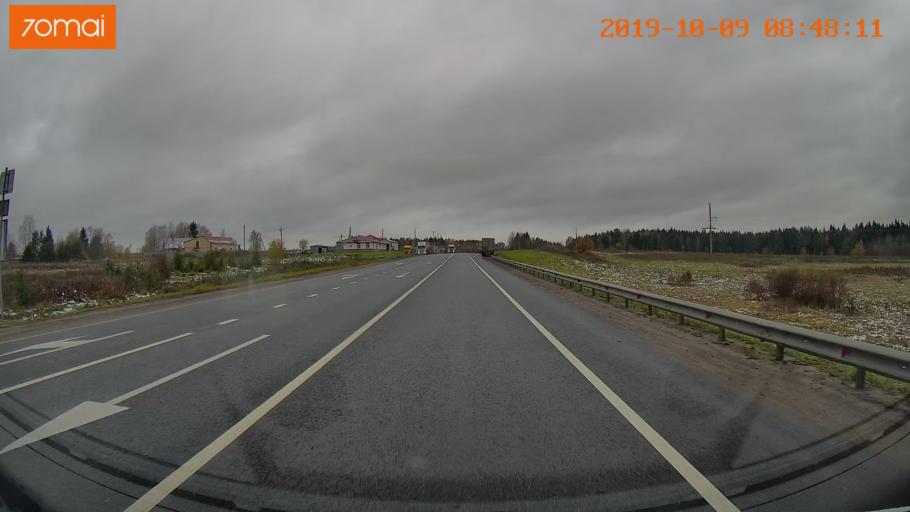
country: RU
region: Vologda
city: Vologda
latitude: 59.0715
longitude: 40.0299
